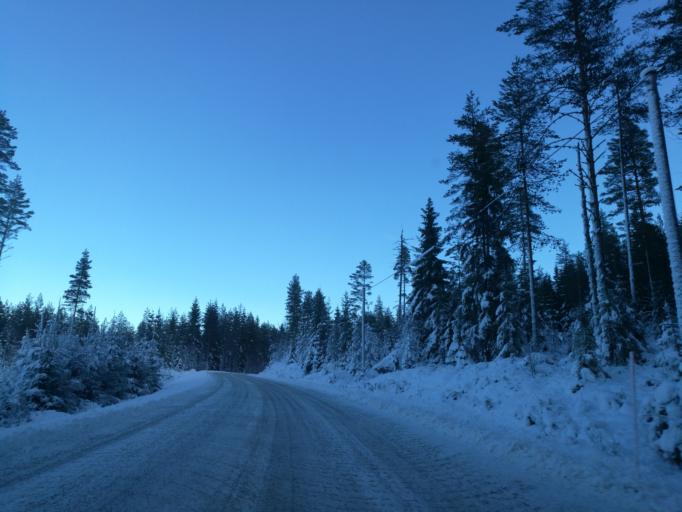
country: NO
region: Hedmark
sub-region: Grue
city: Kirkenaer
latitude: 60.4506
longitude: 12.4733
